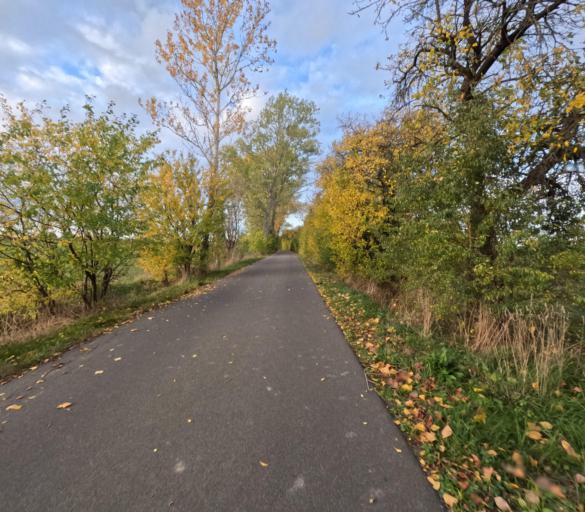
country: DE
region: Saxony
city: Grimma
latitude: 51.2487
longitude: 12.6951
